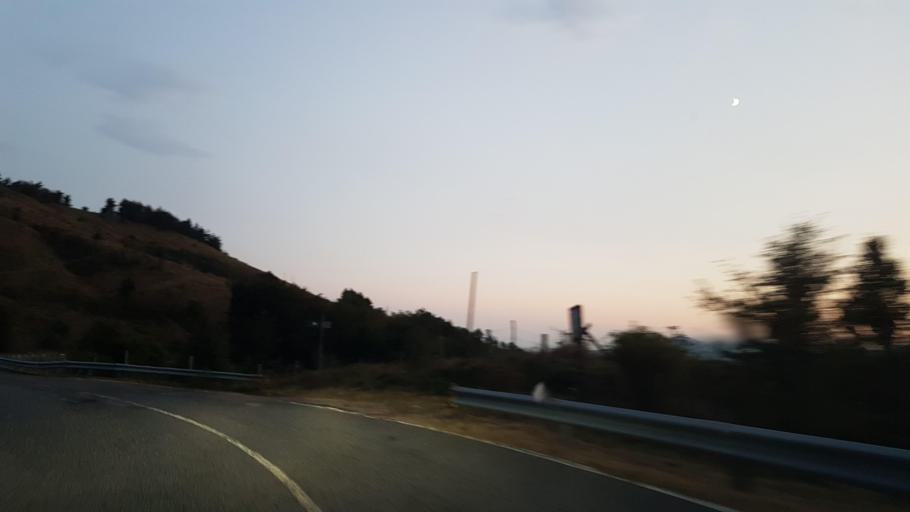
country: IT
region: Liguria
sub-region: Provincia di La Spezia
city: Varese Ligure
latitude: 44.4053
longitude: 9.6196
